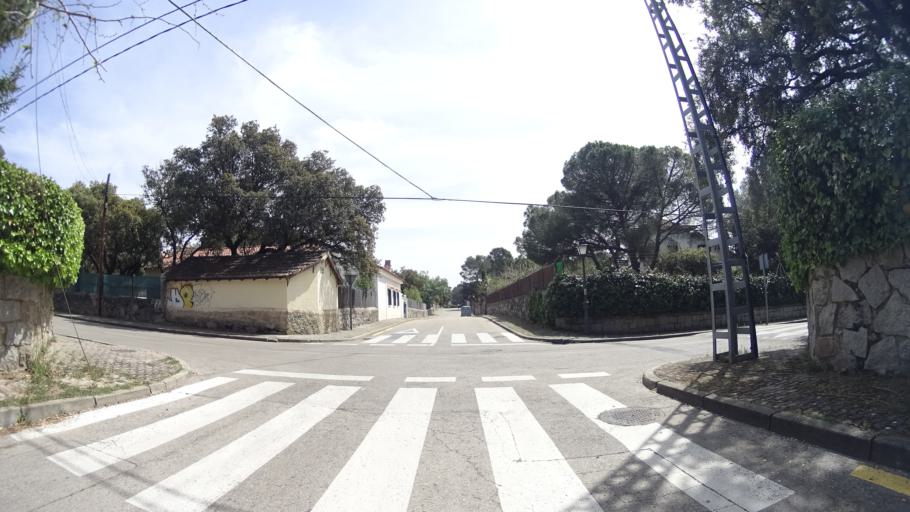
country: ES
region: Madrid
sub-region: Provincia de Madrid
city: Torrelodones
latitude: 40.5823
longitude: -3.9572
